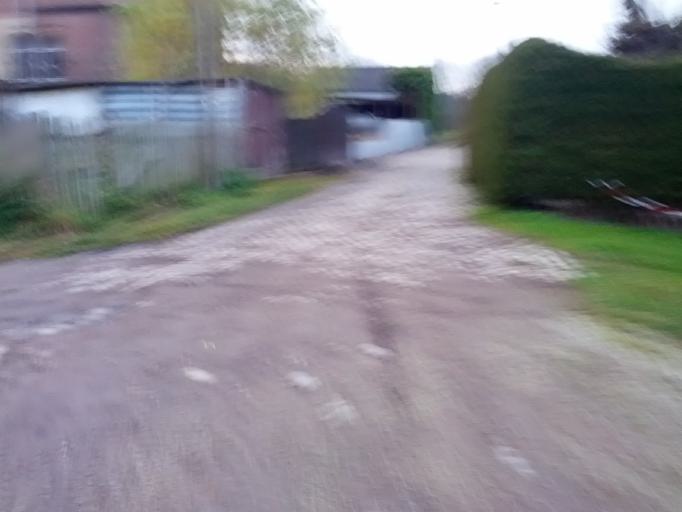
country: DE
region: Thuringia
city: Eisenach
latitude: 50.9622
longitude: 10.3642
